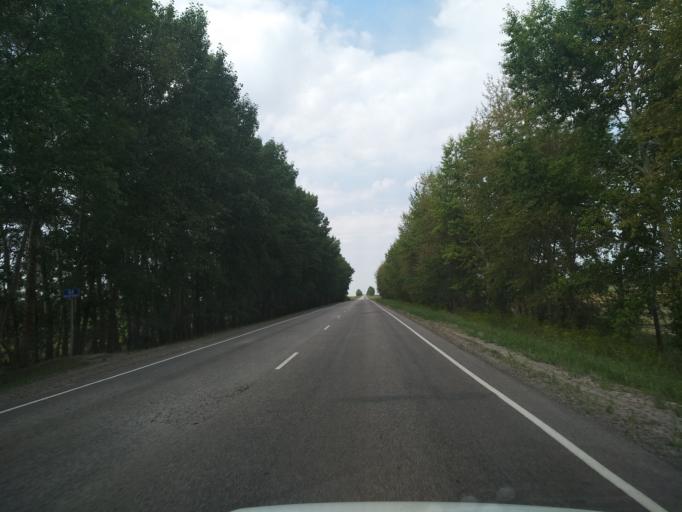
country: RU
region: Voronezj
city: Pereleshino
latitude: 51.7273
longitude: 40.0491
